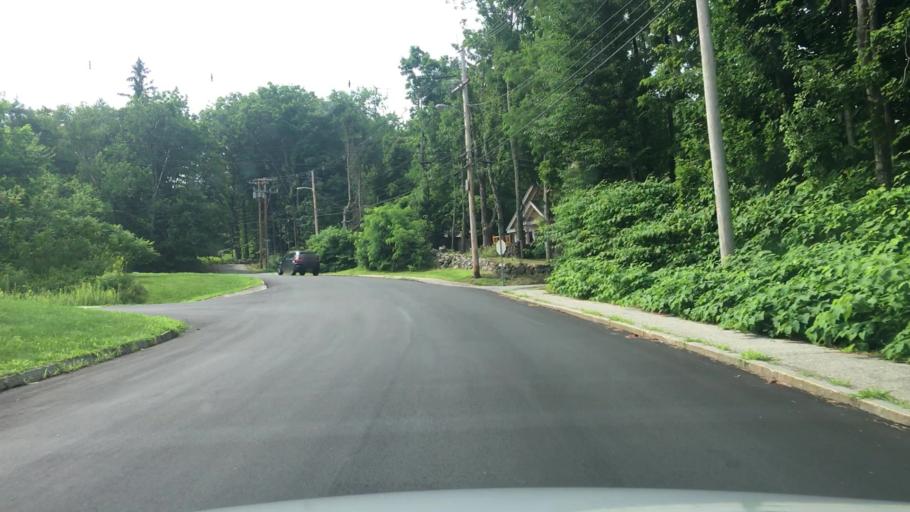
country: US
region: New Hampshire
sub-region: Belknap County
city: Meredith
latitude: 43.6487
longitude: -71.5011
